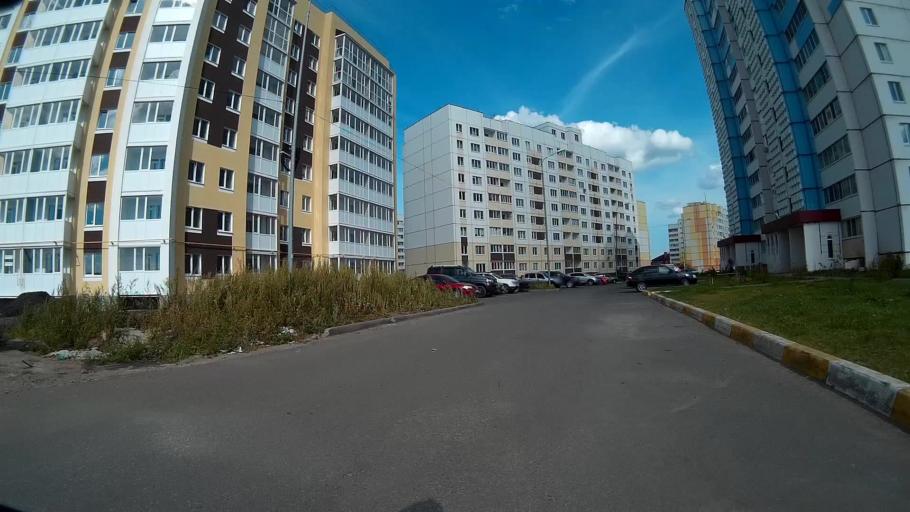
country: RU
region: Ulyanovsk
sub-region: Ulyanovskiy Rayon
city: Ulyanovsk
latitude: 54.2780
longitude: 48.2660
